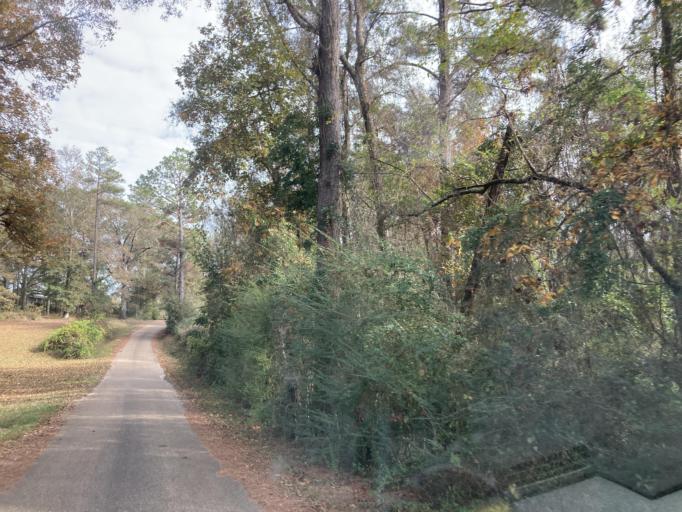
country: US
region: Mississippi
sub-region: Lamar County
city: Purvis
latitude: 31.2233
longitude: -89.3736
